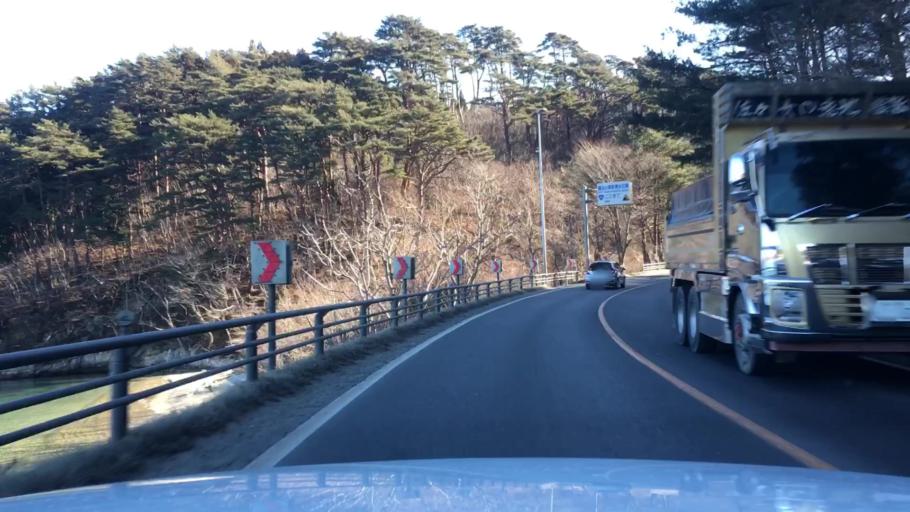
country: JP
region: Iwate
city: Yamada
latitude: 39.4476
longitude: 141.9669
